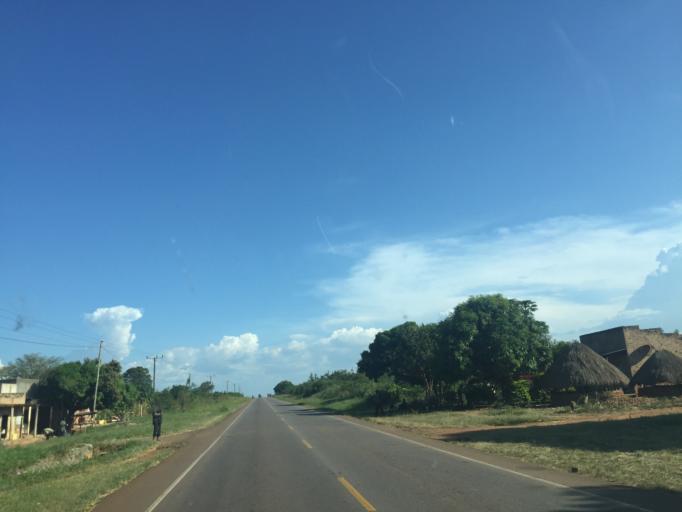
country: UG
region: Central Region
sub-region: Nakasongola District
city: Nakasongola
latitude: 1.2853
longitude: 32.4320
